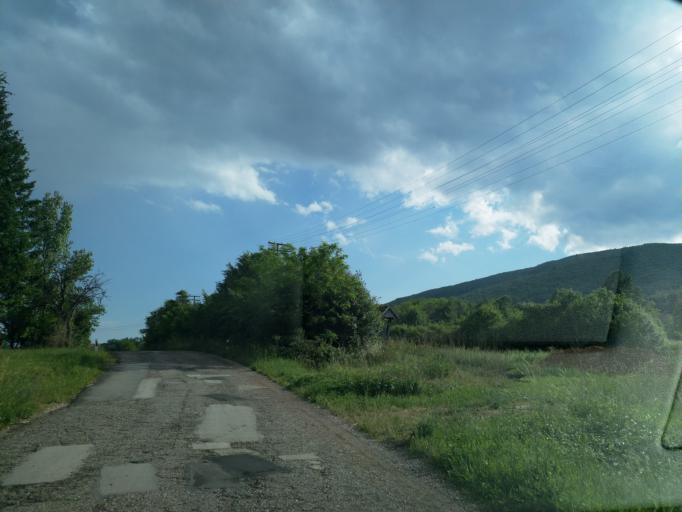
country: RS
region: Central Serbia
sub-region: Borski Okrug
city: Bor
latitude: 43.9903
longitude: 21.9751
